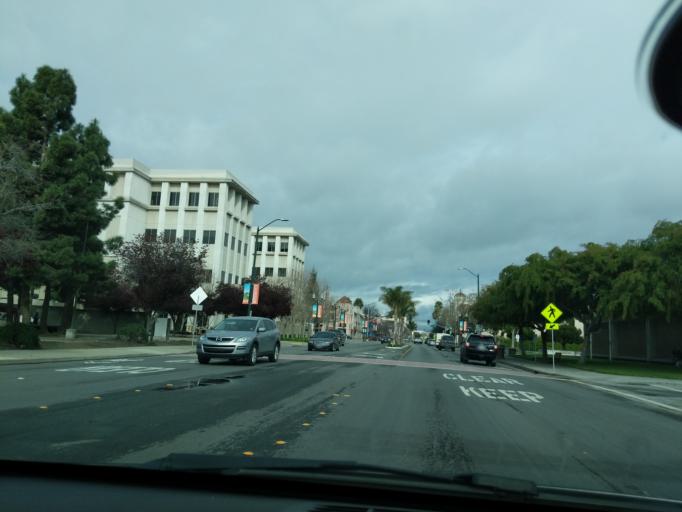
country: US
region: California
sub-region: Santa Cruz County
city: Watsonville
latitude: 36.9082
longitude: -121.7545
